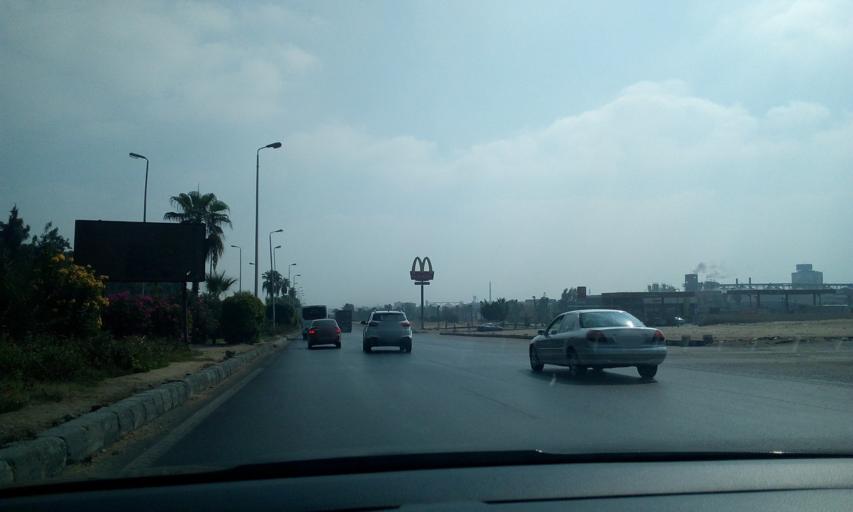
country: EG
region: Eastern Province
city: Bilbays
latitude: 30.2447
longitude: 31.7258
